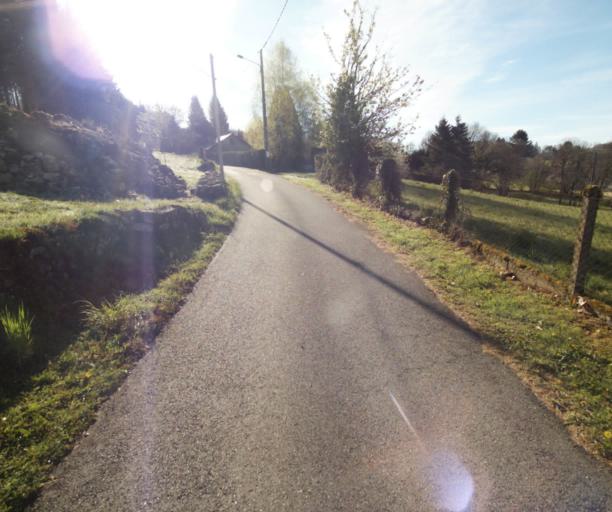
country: FR
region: Limousin
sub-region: Departement de la Correze
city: Laguenne
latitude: 45.2858
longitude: 1.8502
